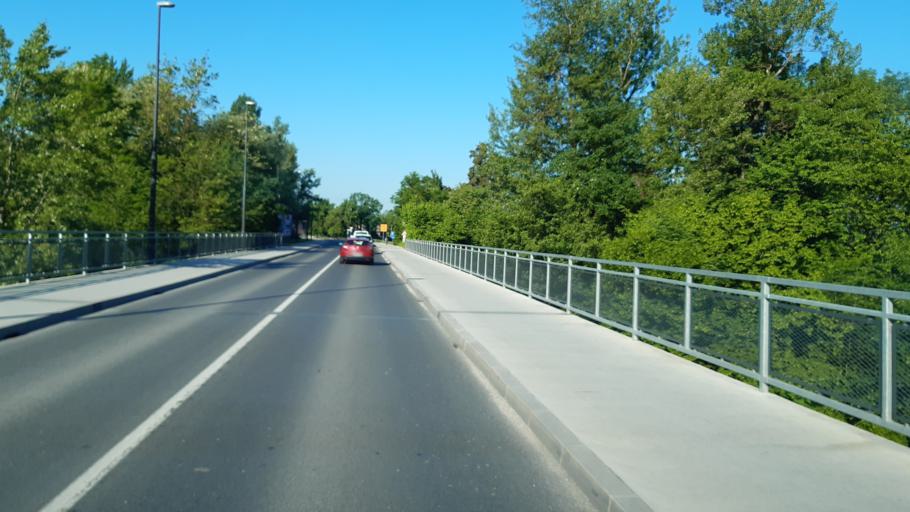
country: SI
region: Ljubljana
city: Ljubljana
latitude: 46.1006
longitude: 14.5190
